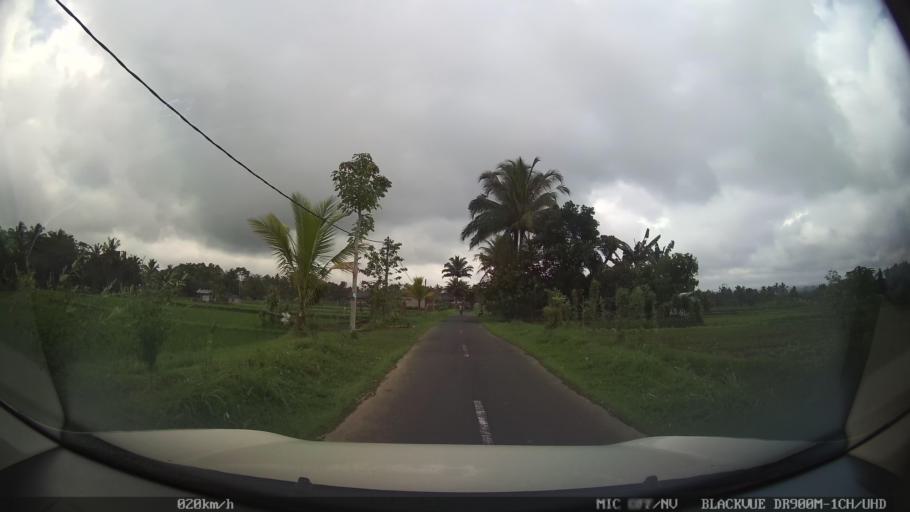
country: ID
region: Bali
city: Badung
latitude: -8.4203
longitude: 115.2270
